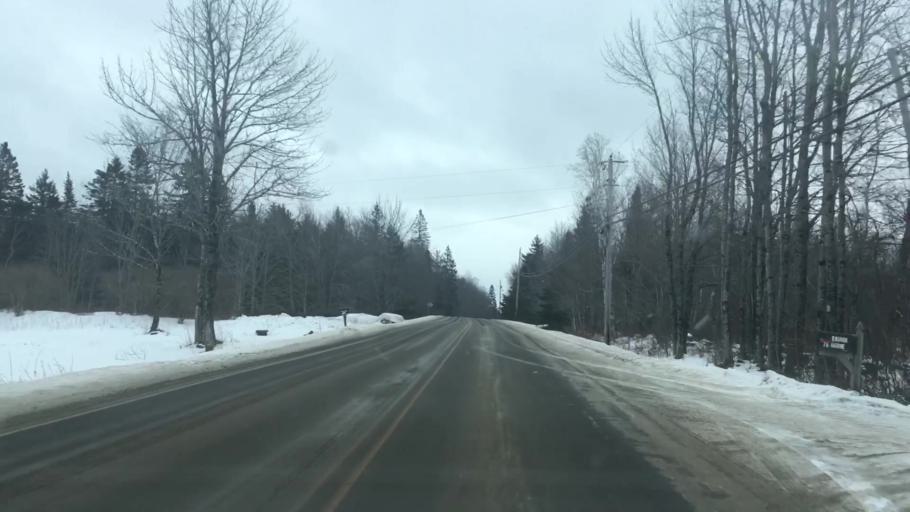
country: US
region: Maine
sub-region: Washington County
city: East Machias
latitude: 44.9860
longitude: -67.4577
